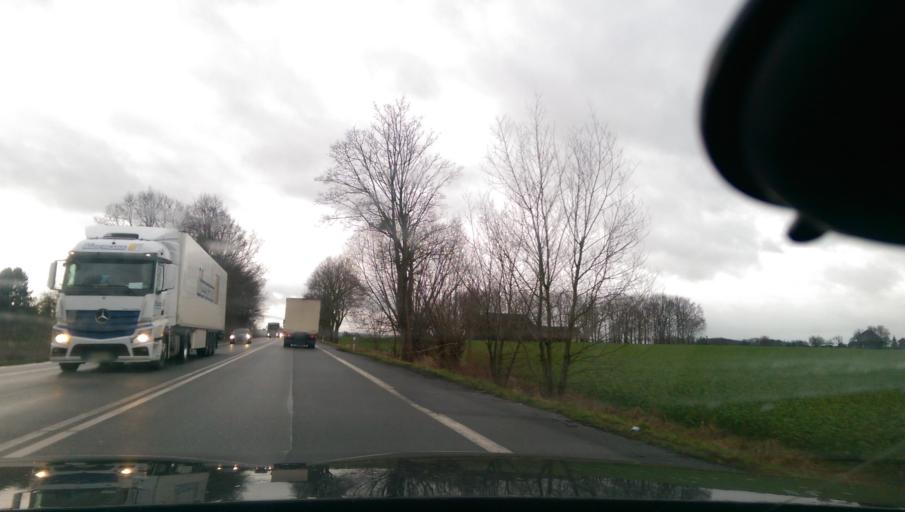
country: DE
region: North Rhine-Westphalia
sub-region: Regierungsbezirk Arnsberg
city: Hamm
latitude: 51.6132
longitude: 7.8506
